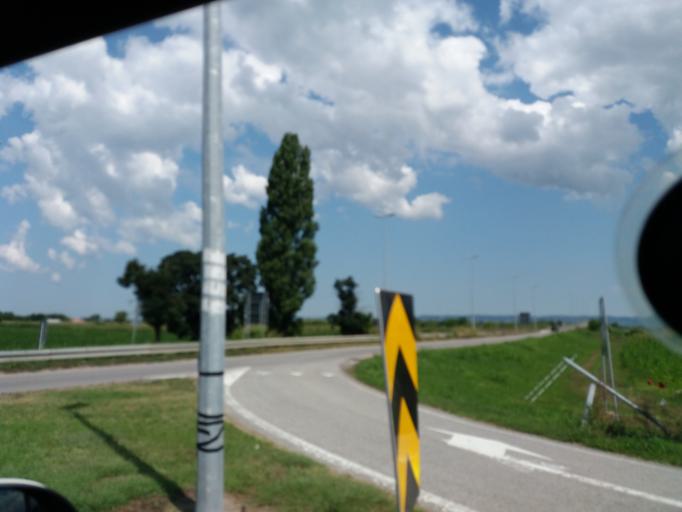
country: RS
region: Autonomna Pokrajina Vojvodina
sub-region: Sremski Okrug
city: Sremska Mitrovica
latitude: 44.9953
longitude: 19.6417
